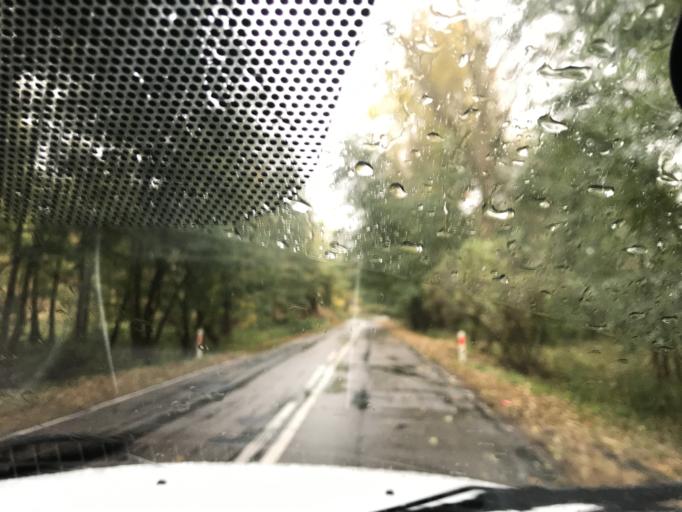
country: DE
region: Brandenburg
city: Neulewin
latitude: 52.7797
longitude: 14.2942
